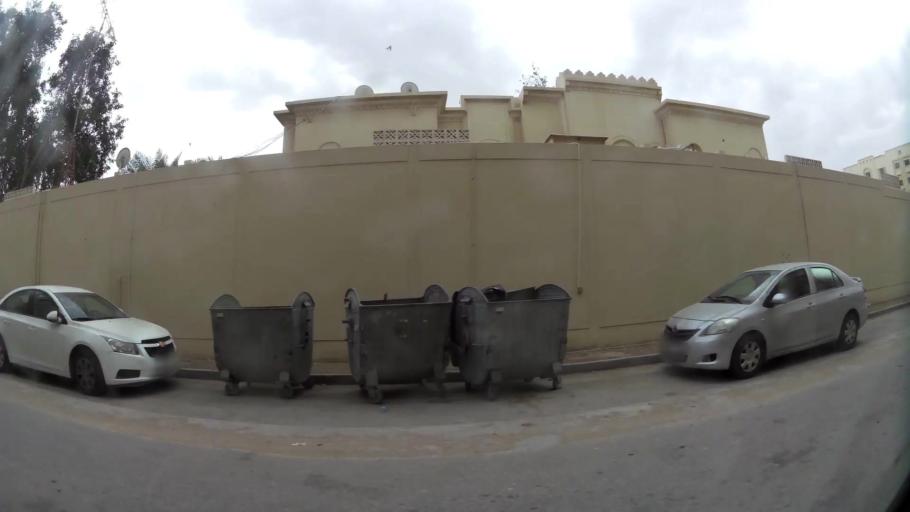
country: QA
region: Baladiyat ad Dawhah
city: Doha
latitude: 25.2785
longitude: 51.5038
